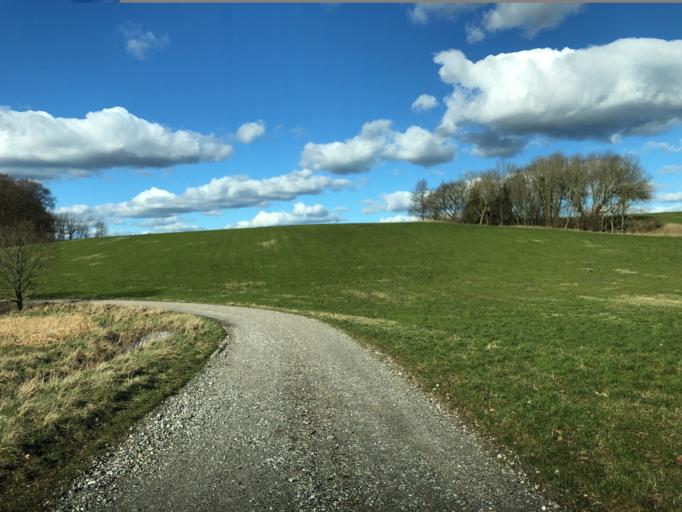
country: DK
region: Central Jutland
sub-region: Favrskov Kommune
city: Hammel
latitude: 56.3056
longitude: 9.9184
